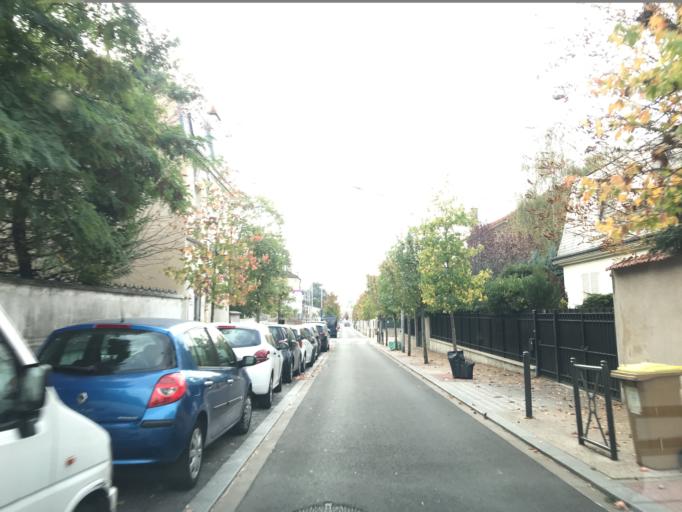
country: FR
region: Ile-de-France
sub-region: Departement du Val-de-Marne
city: Le Perreux-sur-Marne
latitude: 48.8389
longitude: 2.5060
